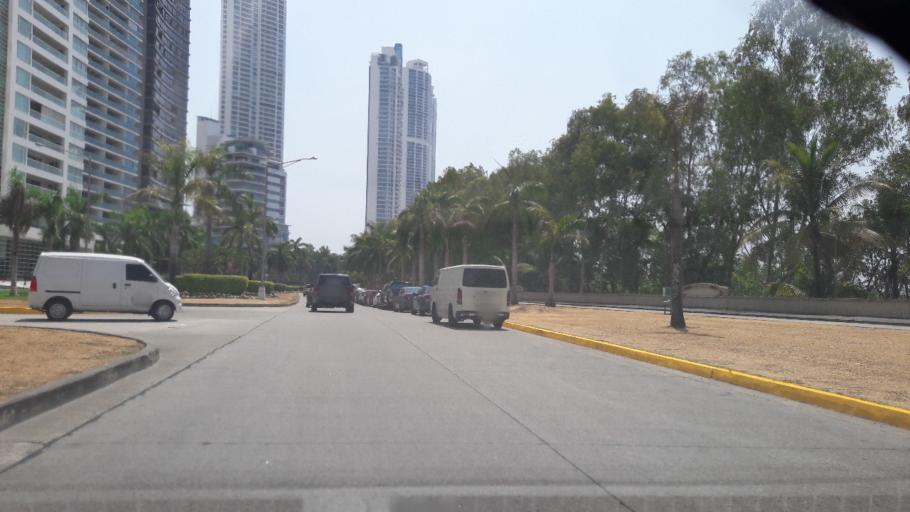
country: PA
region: Panama
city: San Miguelito
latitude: 9.0088
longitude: -79.4726
